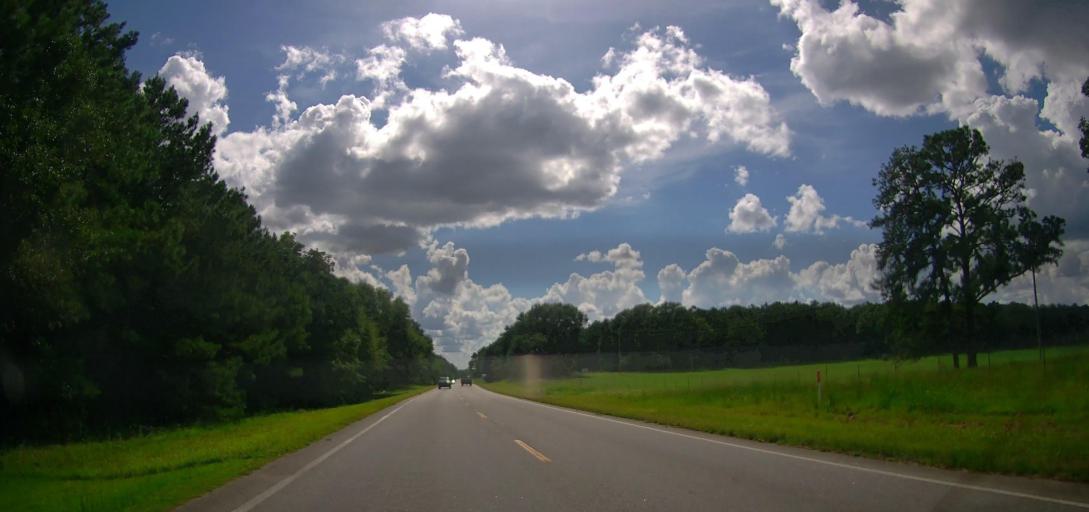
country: US
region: Alabama
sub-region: Lee County
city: Opelika
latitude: 32.4414
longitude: -85.2981
